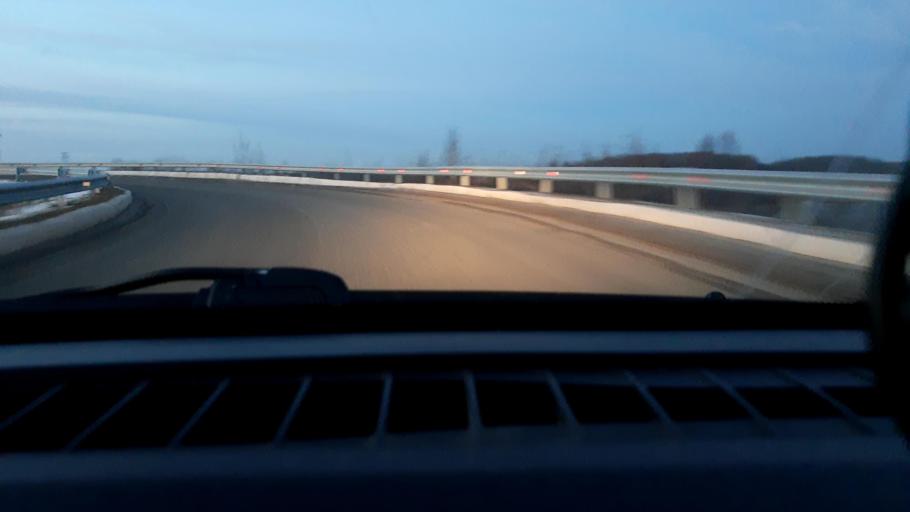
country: RU
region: Nizjnij Novgorod
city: Gorbatovka
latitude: 56.2827
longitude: 43.8410
